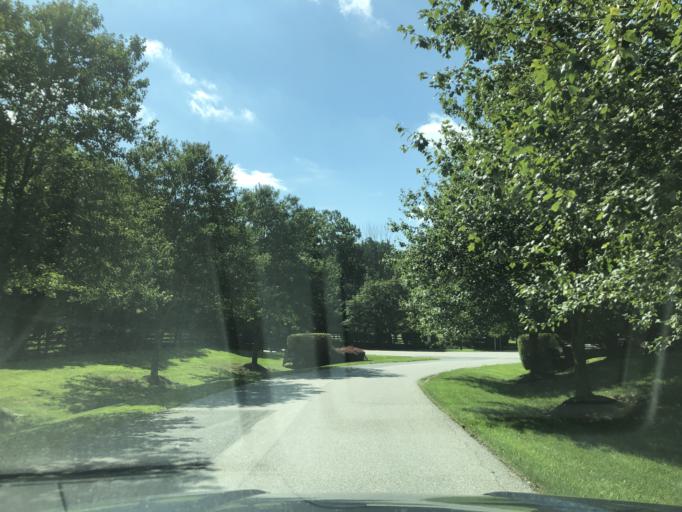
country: US
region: Maryland
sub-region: Howard County
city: Highland
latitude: 39.2023
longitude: -76.9746
